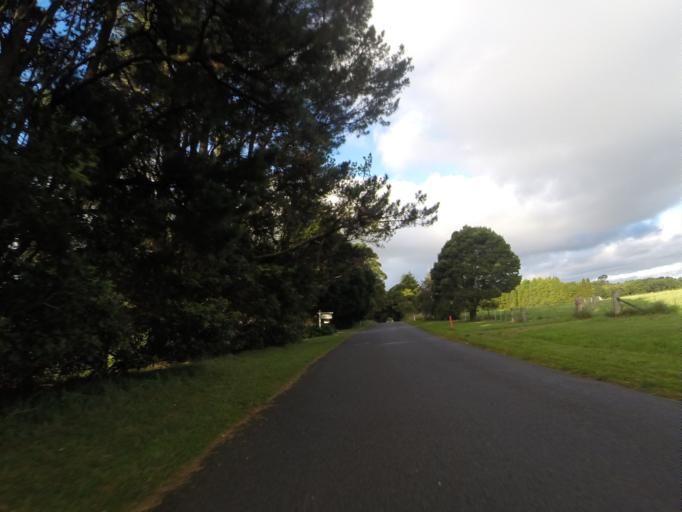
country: AU
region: New South Wales
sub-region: Shoalhaven Shire
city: Kangaroo Valley
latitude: -34.6034
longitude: 150.5463
